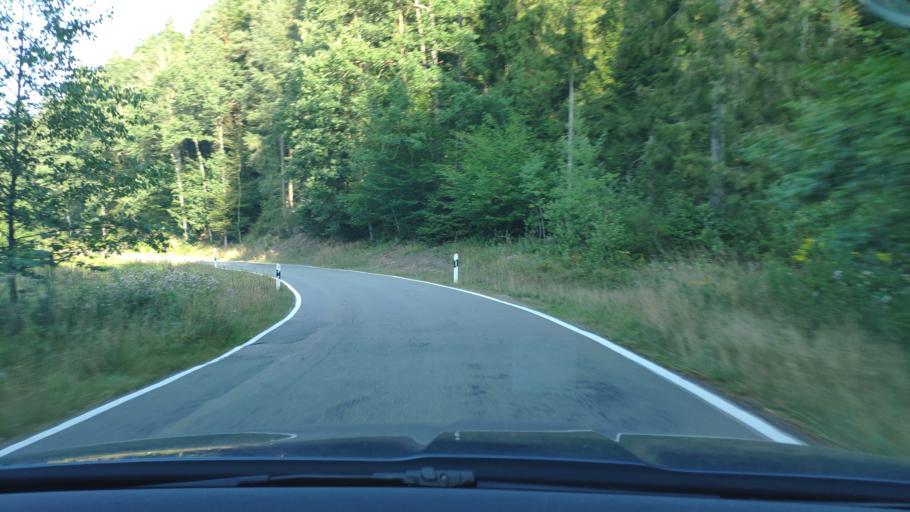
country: DE
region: Rheinland-Pfalz
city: Ludwigswinkel
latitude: 49.0904
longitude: 7.6507
